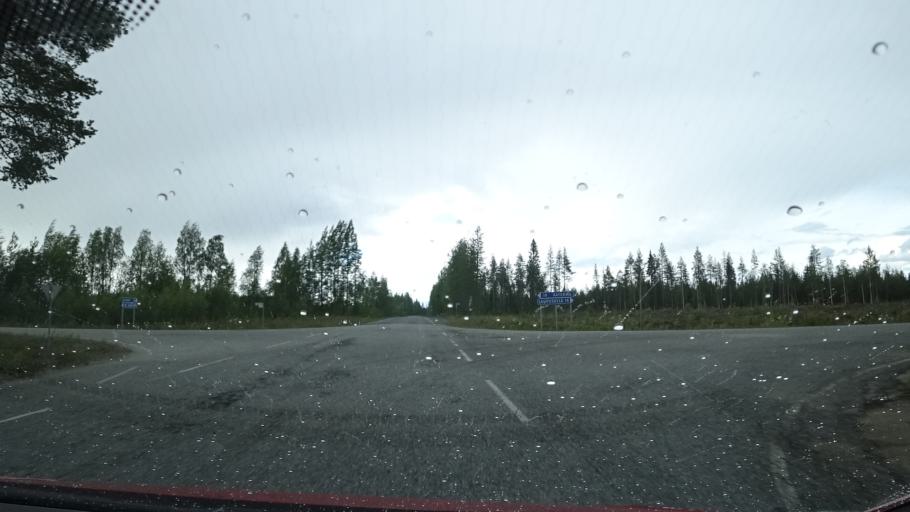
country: FI
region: Kainuu
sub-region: Kehys-Kainuu
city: Kuhmo
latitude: 63.9794
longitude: 29.2629
